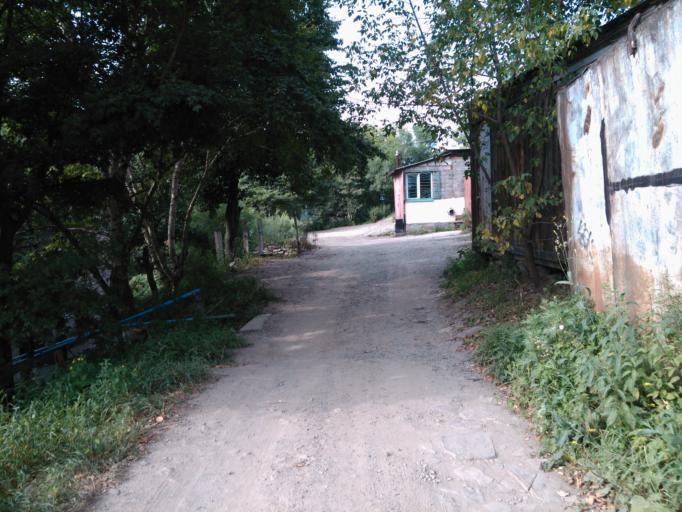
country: RU
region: Primorskiy
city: Vladivostok
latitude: 43.0927
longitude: 131.9598
